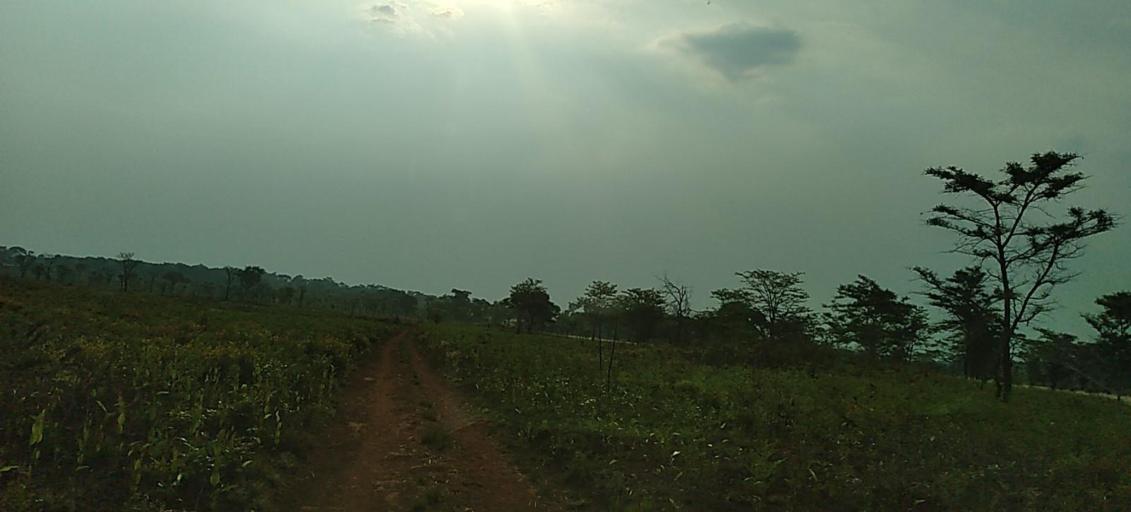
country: ZM
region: North-Western
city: Solwezi
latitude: -12.0466
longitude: 26.0647
